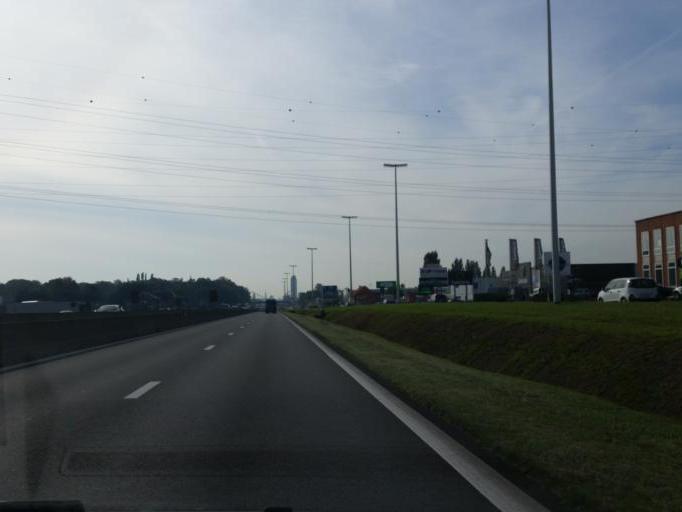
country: BE
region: Flanders
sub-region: Provincie Antwerpen
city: Aartselaar
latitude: 51.1191
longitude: 4.3729
